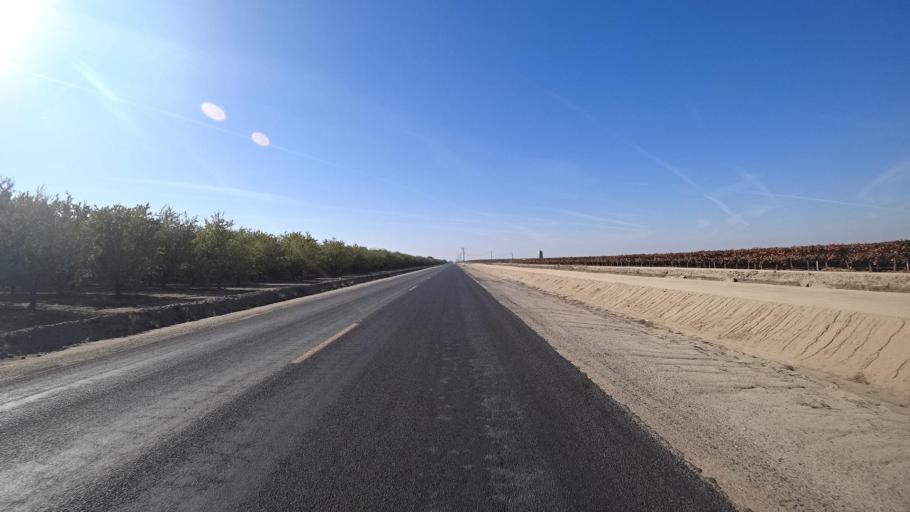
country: US
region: California
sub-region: Kern County
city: McFarland
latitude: 35.6453
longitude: -119.2877
